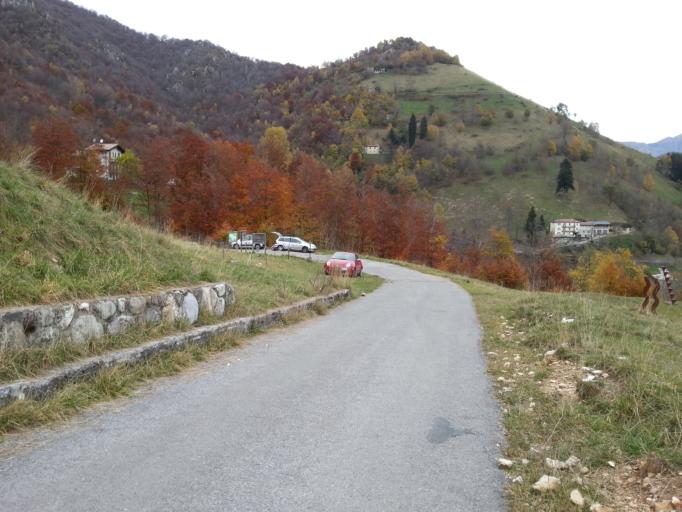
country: IT
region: Lombardy
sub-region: Provincia di Lecco
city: Morterone
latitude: 45.8731
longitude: 9.4820
